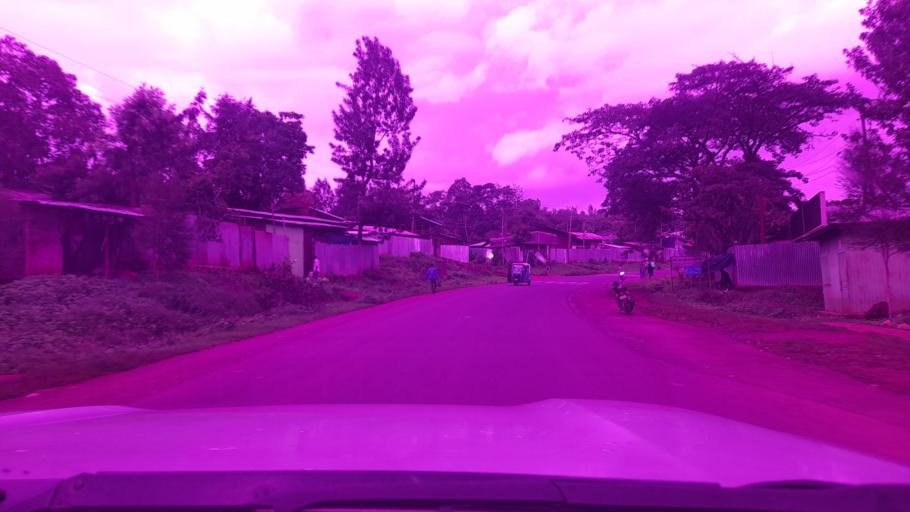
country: ET
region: Oromiya
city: Jima
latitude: 7.9276
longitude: 37.4218
